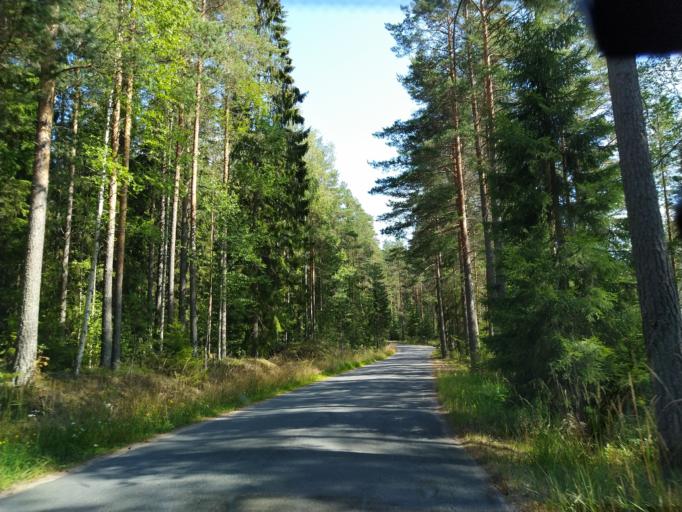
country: FI
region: Uusimaa
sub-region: Helsinki
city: Karkkila
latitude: 60.7180
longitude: 24.1937
